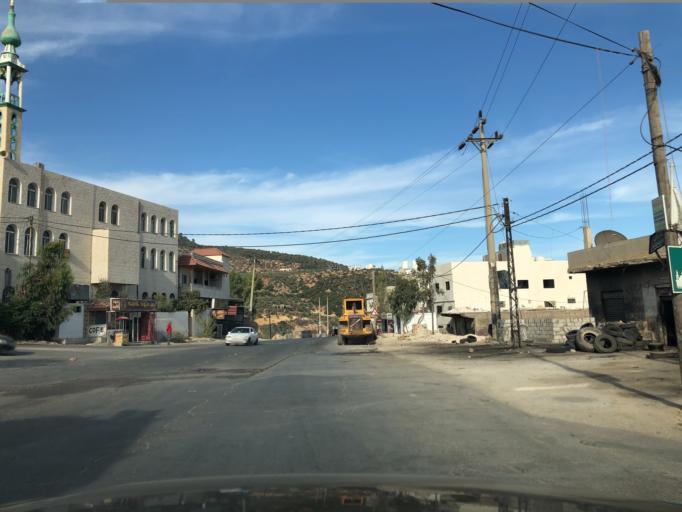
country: JO
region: Irbid
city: Sakib
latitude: 32.2831
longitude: 35.8120
